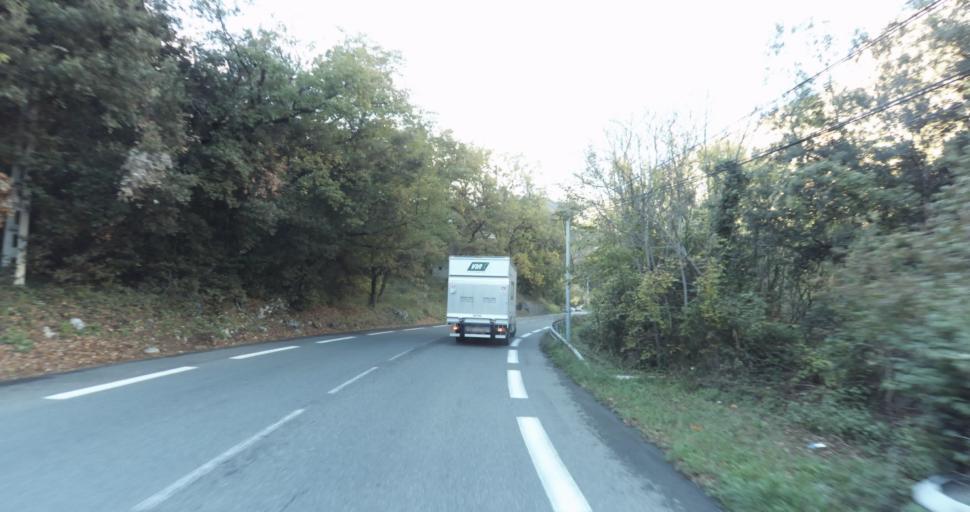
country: FR
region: Provence-Alpes-Cote d'Azur
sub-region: Departement des Alpes-Maritimes
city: Saint-Jeannet
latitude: 43.7470
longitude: 7.1305
